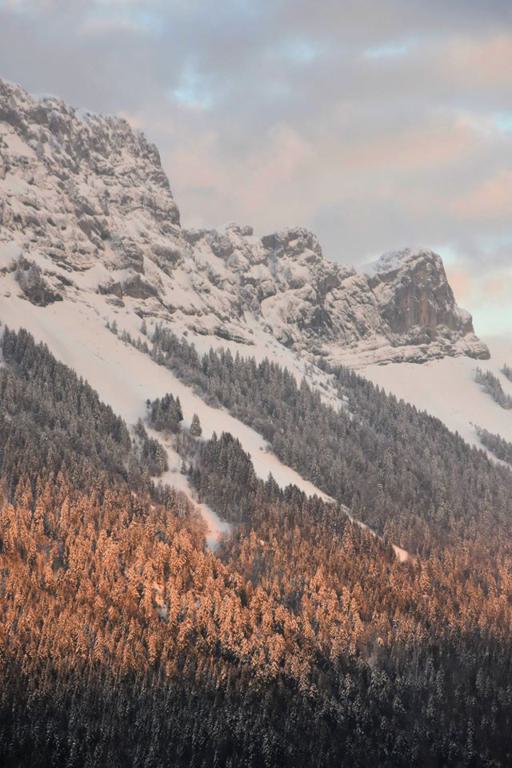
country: FR
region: Rhone-Alpes
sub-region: Departement de la Haute-Savoie
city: Doussard
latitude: 45.8097
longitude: 6.2461
